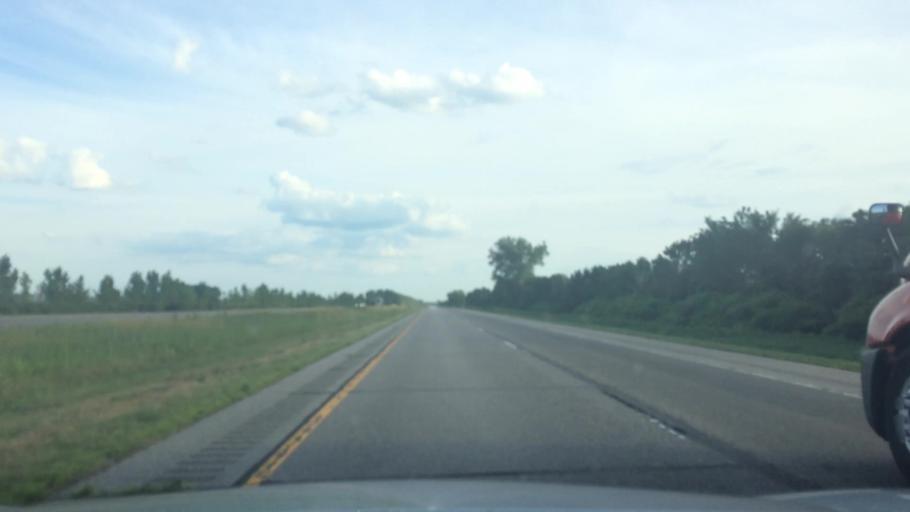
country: US
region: Wisconsin
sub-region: Portage County
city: Plover
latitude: 44.3658
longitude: -89.5204
